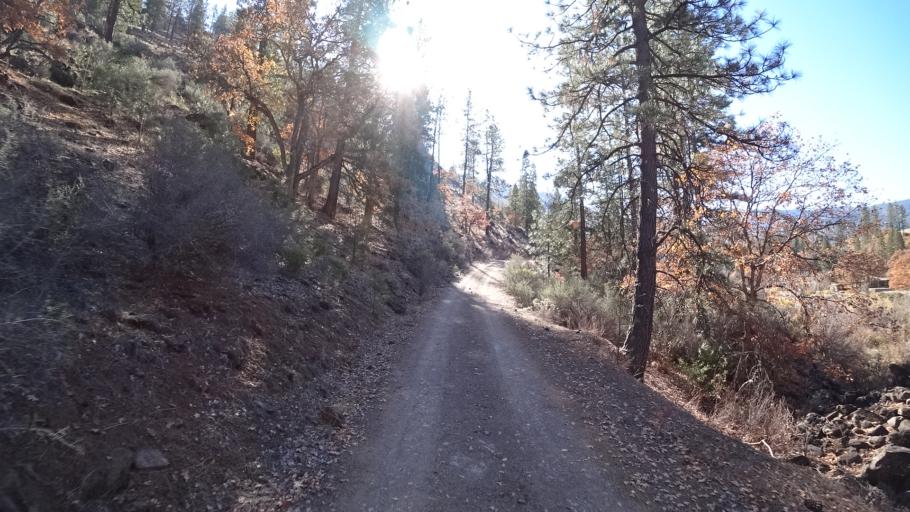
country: US
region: California
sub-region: Siskiyou County
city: Yreka
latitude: 41.8631
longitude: -122.7445
